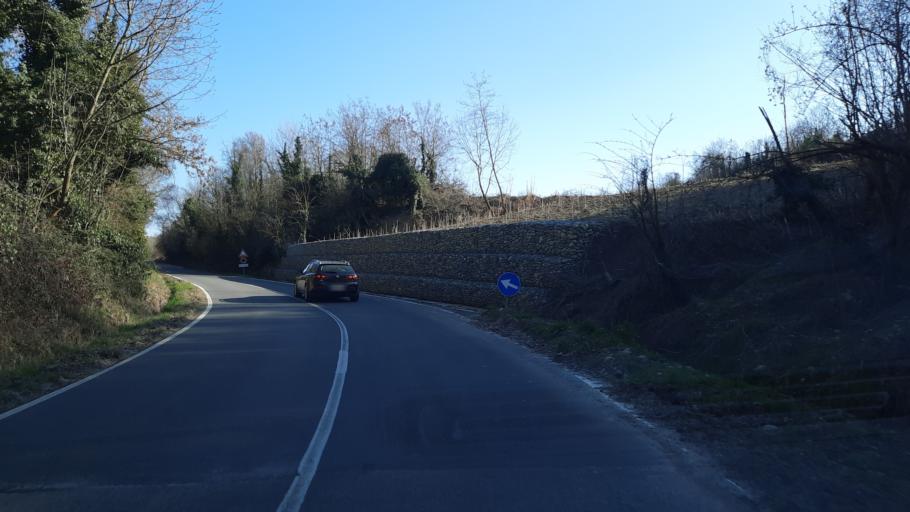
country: IT
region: Piedmont
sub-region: Provincia di Alessandria
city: Camino
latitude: 45.1726
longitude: 8.2800
